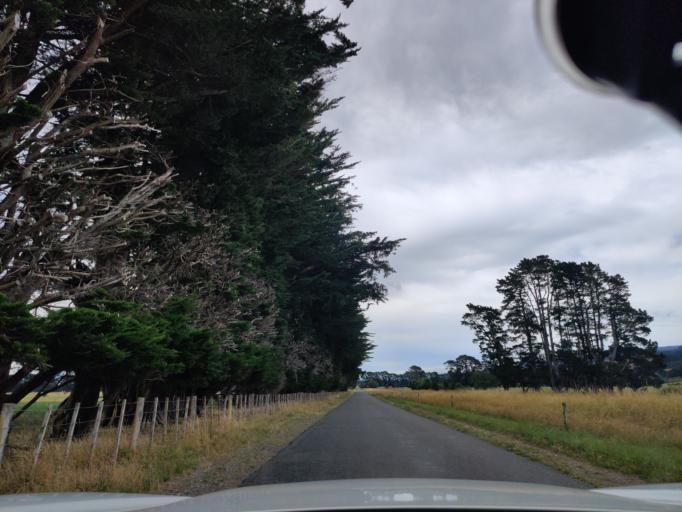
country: NZ
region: Wellington
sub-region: Masterton District
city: Masterton
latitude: -41.0186
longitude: 175.4646
